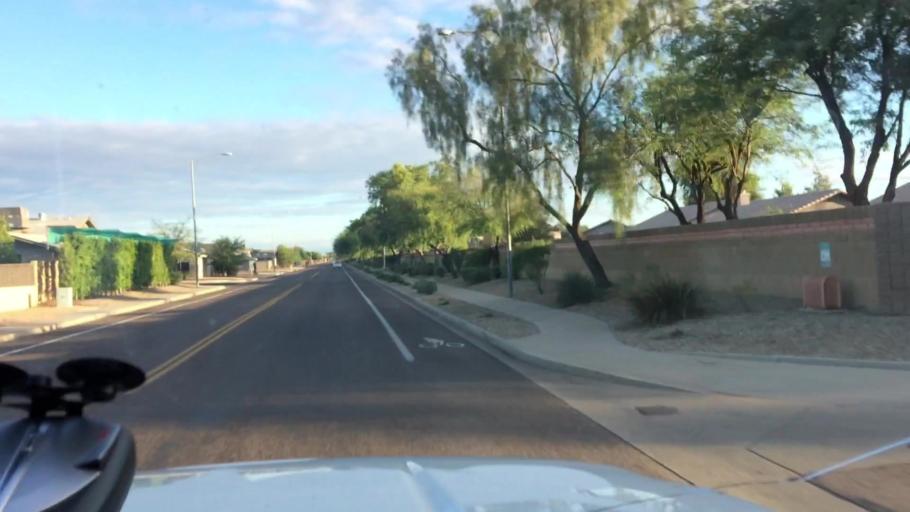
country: US
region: Arizona
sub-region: Maricopa County
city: Sun City
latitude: 33.5709
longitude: -112.2638
